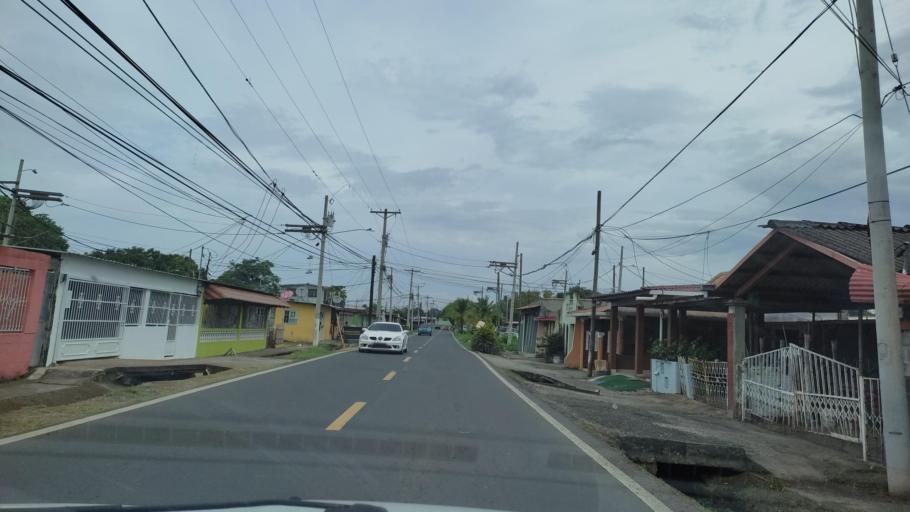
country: PA
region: Panama
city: San Miguelito
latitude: 9.0489
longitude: -79.4324
